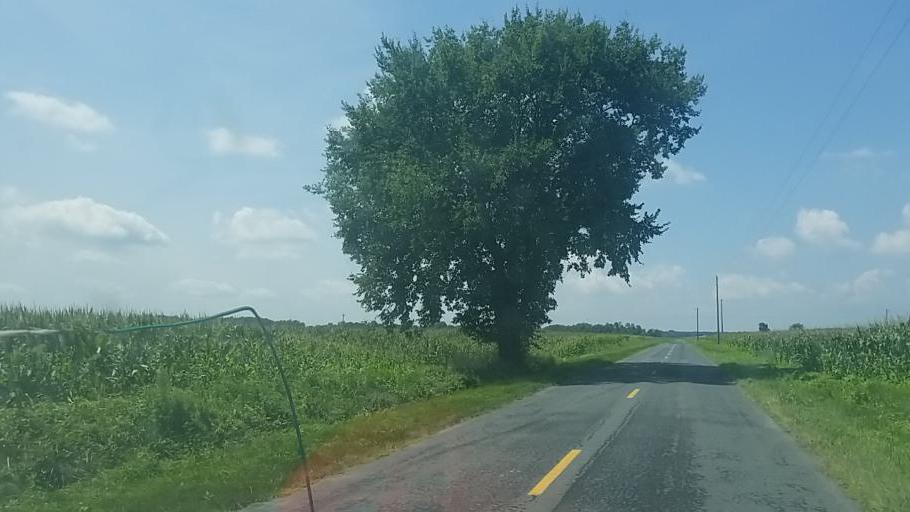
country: US
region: Maryland
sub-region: Talbot County
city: Easton
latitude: 38.7829
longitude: -75.9981
